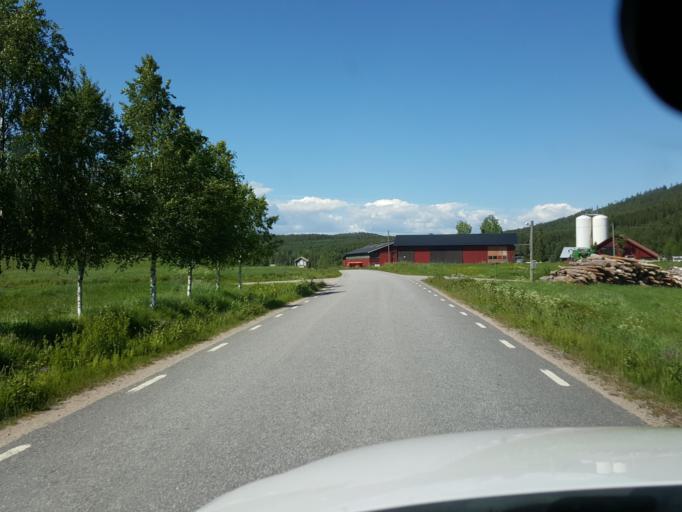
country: SE
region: Gaevleborg
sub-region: Ljusdals Kommun
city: Jaervsoe
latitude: 61.7368
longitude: 16.2794
